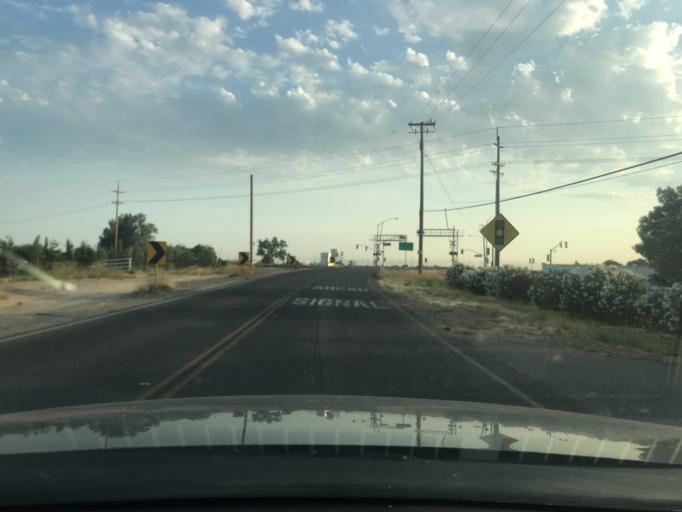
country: US
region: California
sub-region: Merced County
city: Merced
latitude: 37.3391
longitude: -120.5407
